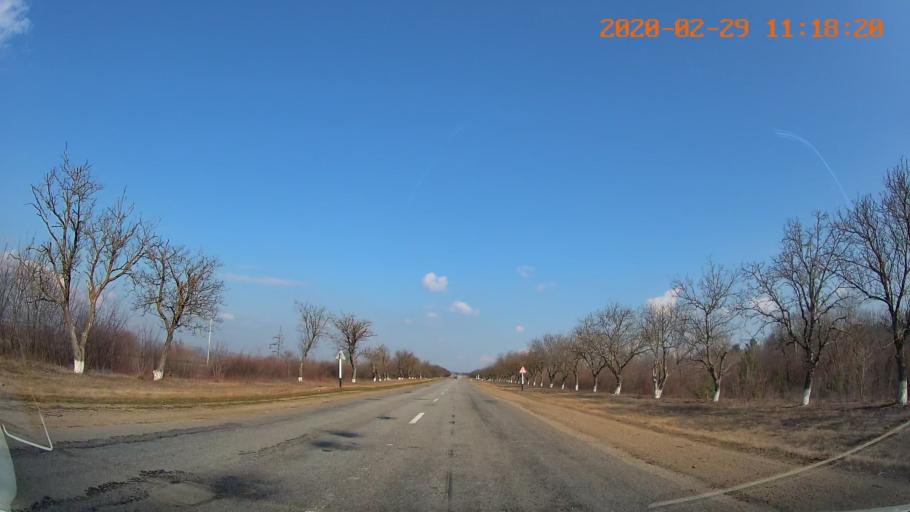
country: MD
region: Telenesti
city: Cocieri
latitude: 47.3335
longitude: 29.1728
